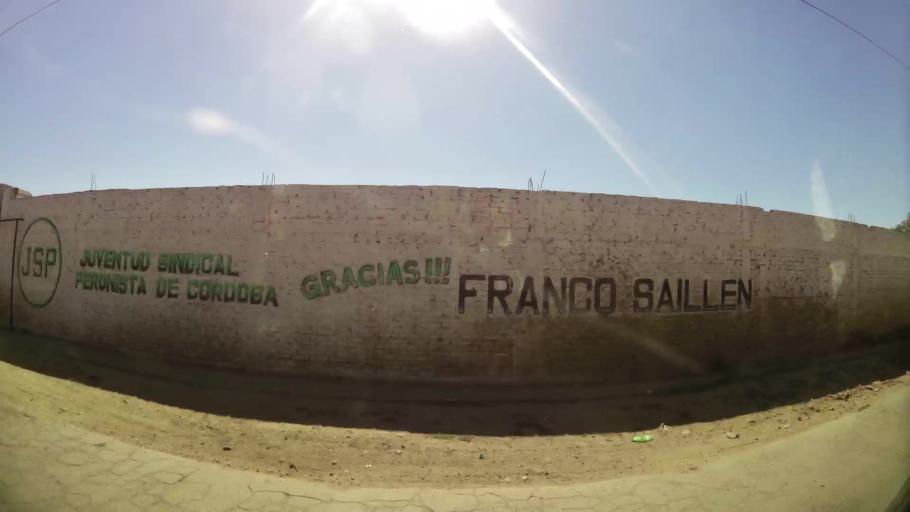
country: AR
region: Cordoba
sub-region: Departamento de Capital
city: Cordoba
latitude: -31.4432
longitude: -64.1345
